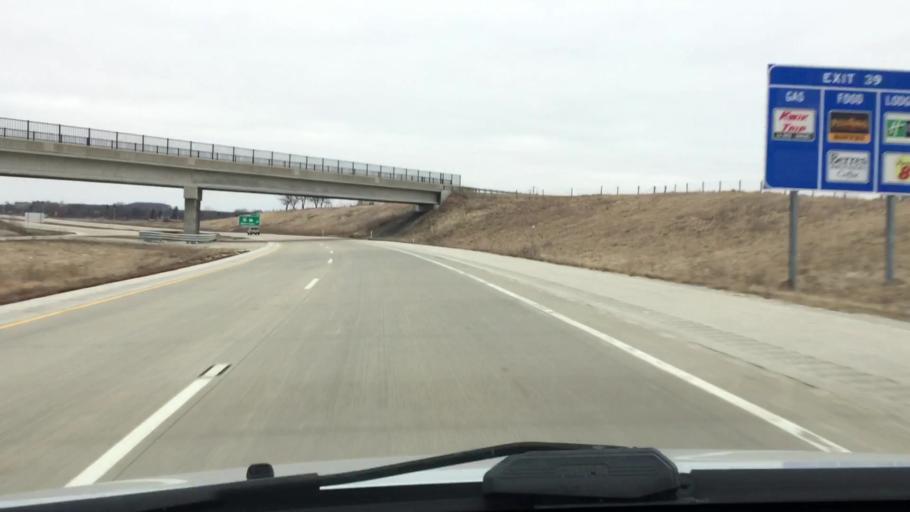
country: US
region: Wisconsin
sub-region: Jefferson County
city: Watertown
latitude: 43.1503
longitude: -88.7349
